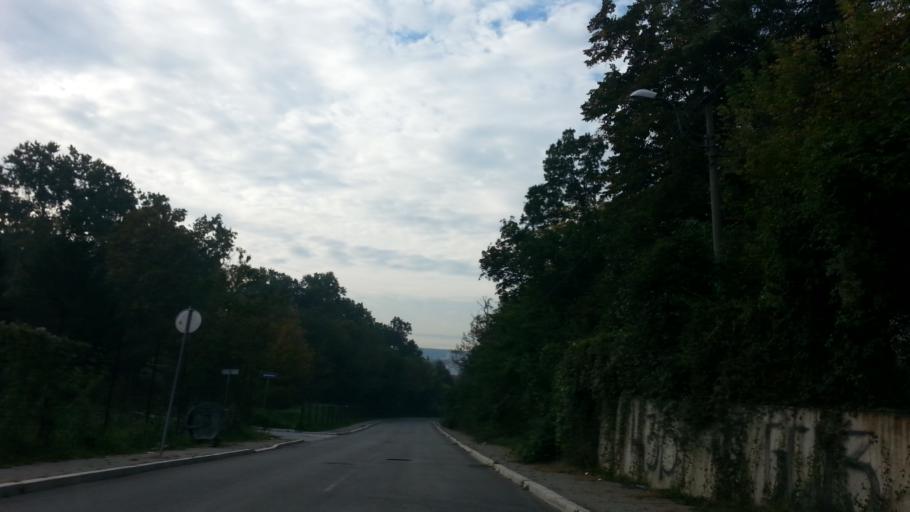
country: RS
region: Central Serbia
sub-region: Belgrade
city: Savski Venac
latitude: 44.7626
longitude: 20.4568
